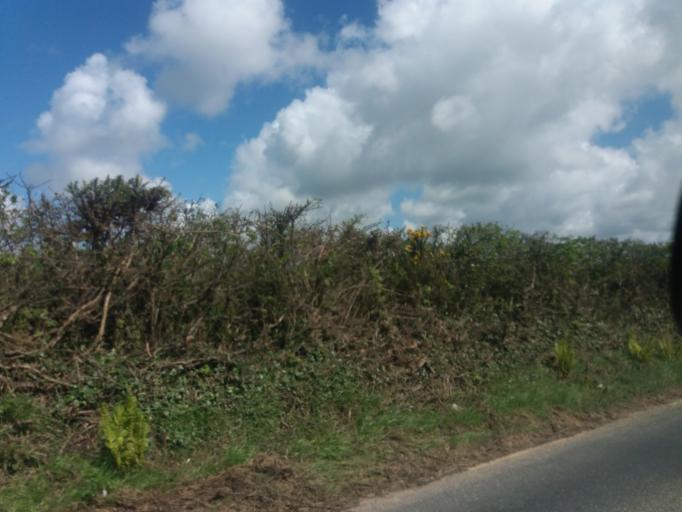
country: IE
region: Leinster
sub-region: Loch Garman
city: Loch Garman
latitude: 52.2831
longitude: -6.6552
